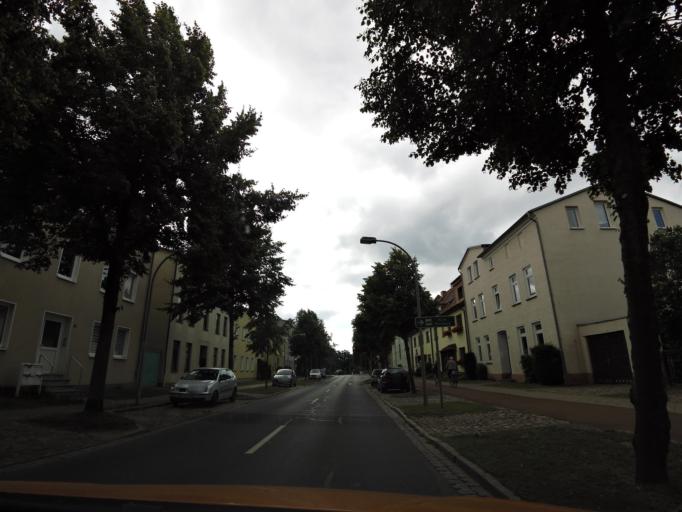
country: DE
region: Mecklenburg-Vorpommern
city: Guestrow
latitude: 53.7853
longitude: 12.1861
